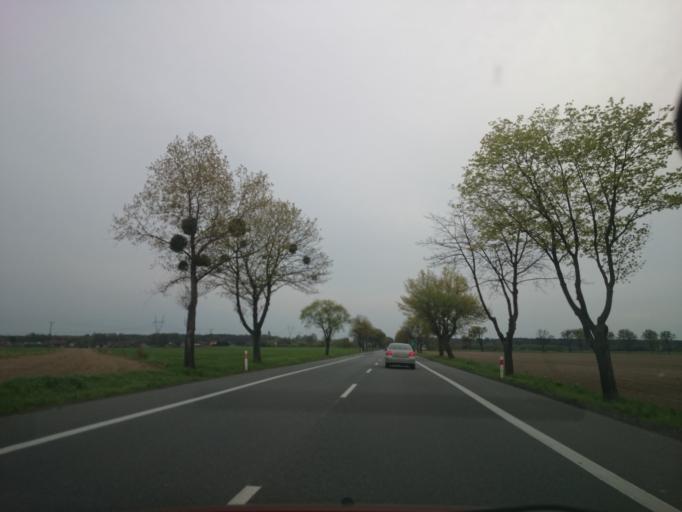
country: PL
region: Opole Voivodeship
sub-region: Powiat opolski
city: Niemodlin
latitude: 50.6240
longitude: 17.5789
